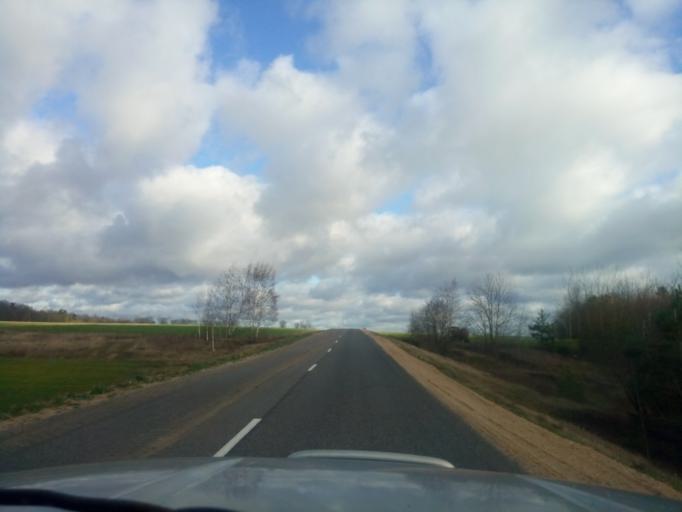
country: BY
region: Minsk
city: Kapyl'
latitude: 53.1449
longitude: 27.0376
